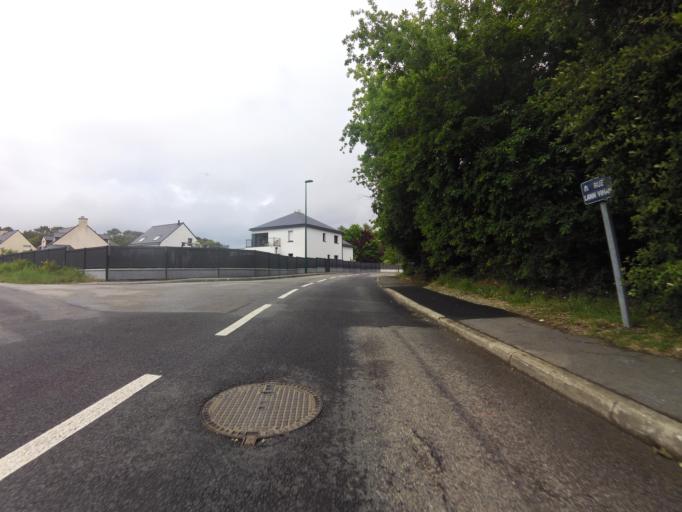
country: FR
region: Brittany
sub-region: Departement du Morbihan
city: Baden
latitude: 47.6151
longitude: -2.9213
